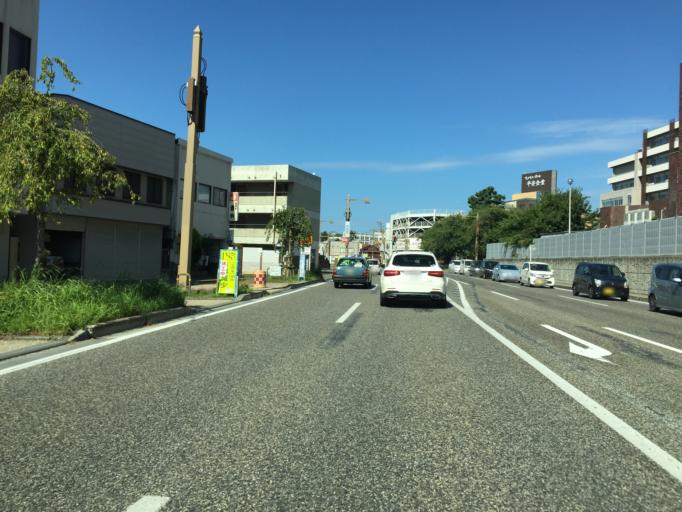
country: JP
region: Niigata
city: Niigata-shi
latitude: 37.9170
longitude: 139.0360
